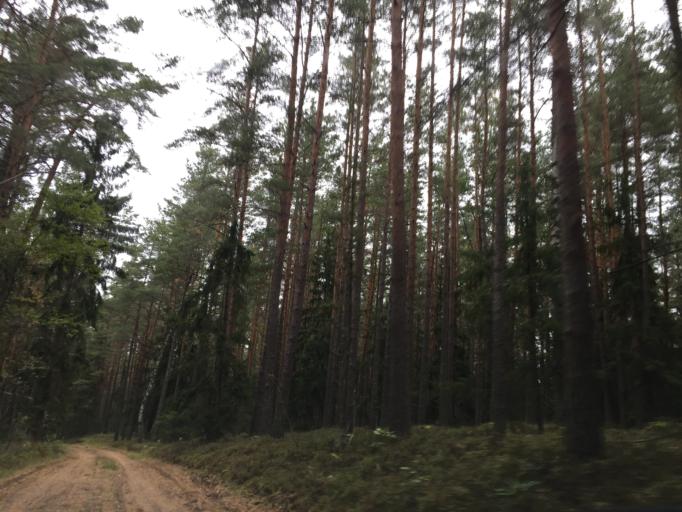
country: LV
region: Salacgrivas
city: Salacgriva
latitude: 57.7064
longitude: 24.3543
